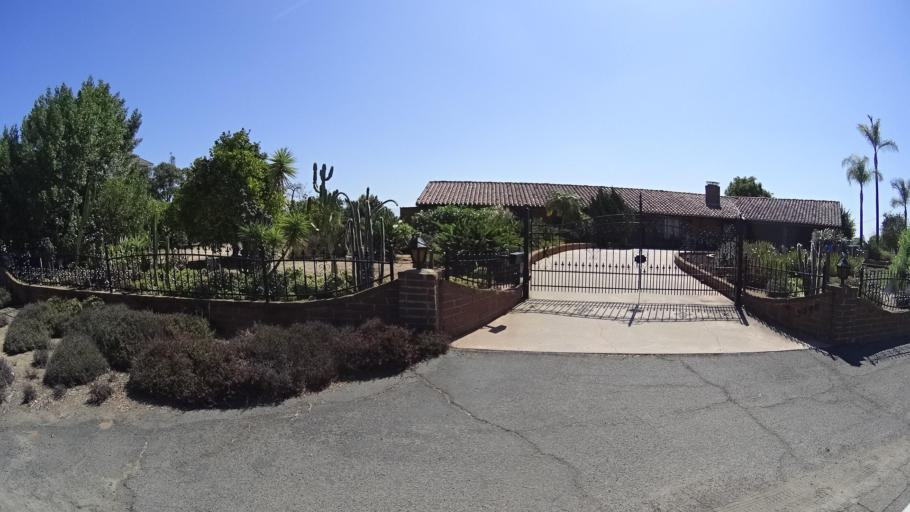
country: US
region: California
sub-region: San Diego County
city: Bonsall
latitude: 33.3287
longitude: -117.2222
